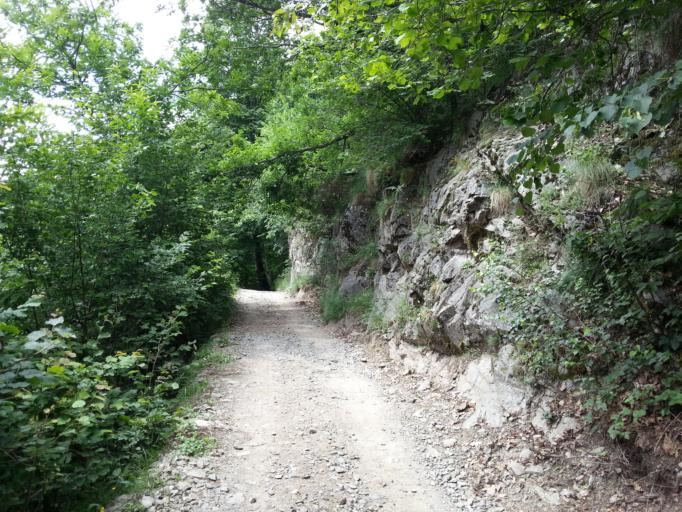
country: IT
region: Lombardy
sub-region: Provincia di Lecco
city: Premana
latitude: 46.0534
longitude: 9.4463
